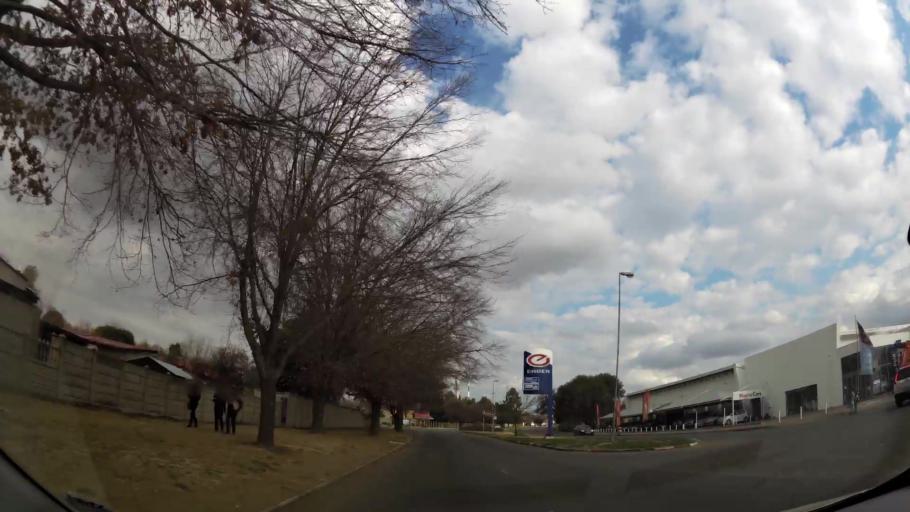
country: ZA
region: Orange Free State
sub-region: Fezile Dabi District Municipality
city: Sasolburg
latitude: -26.8137
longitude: 27.8295
